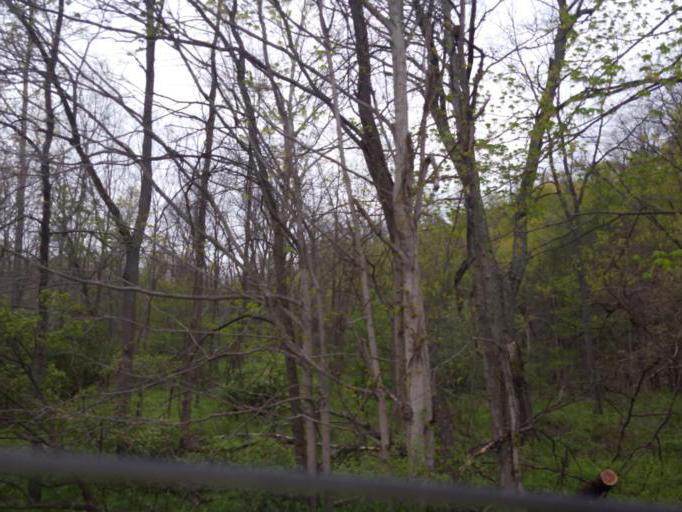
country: US
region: Ohio
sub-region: Richland County
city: Lexington
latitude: 40.7106
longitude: -82.6042
